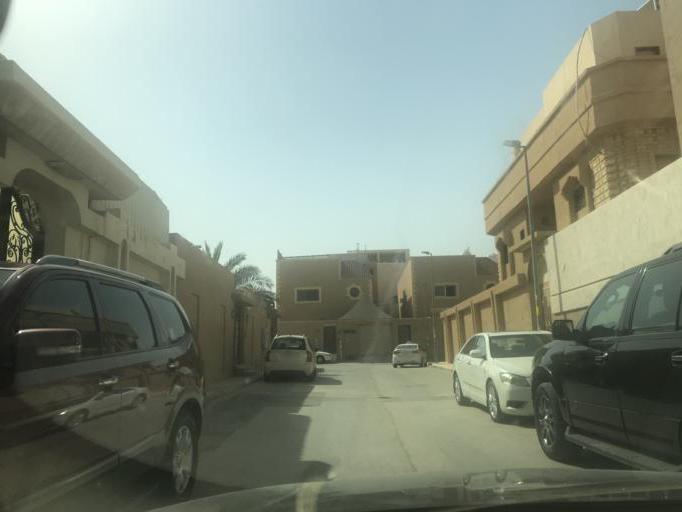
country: SA
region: Ar Riyad
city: Riyadh
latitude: 24.7475
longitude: 46.7655
